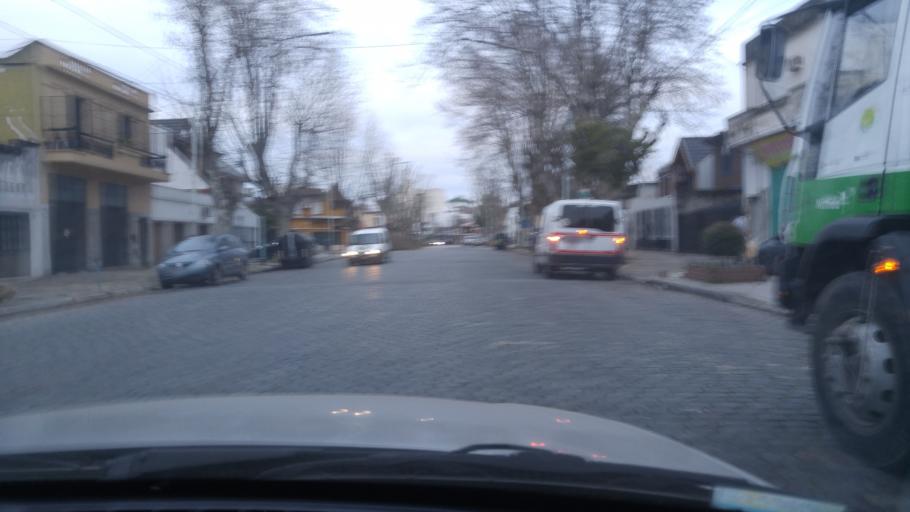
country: AR
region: Buenos Aires F.D.
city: Villa Santa Rita
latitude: -34.6296
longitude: -58.5167
